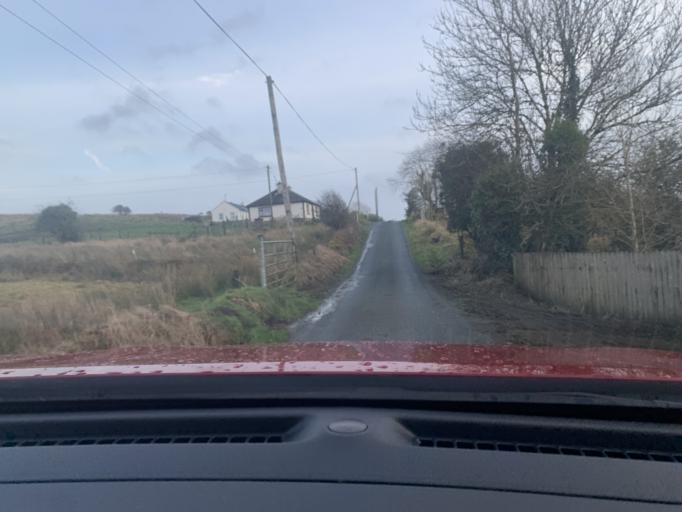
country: IE
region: Connaught
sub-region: Roscommon
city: Ballaghaderreen
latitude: 53.9530
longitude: -8.5238
